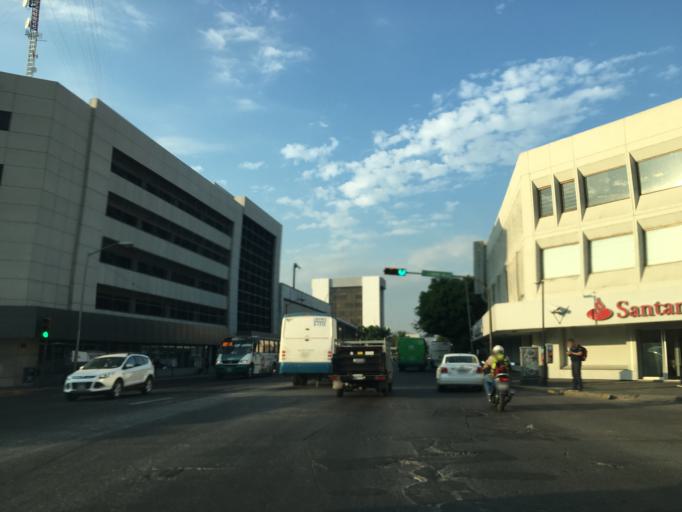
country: MX
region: Jalisco
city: Guadalajara
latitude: 20.6701
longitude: -103.3473
